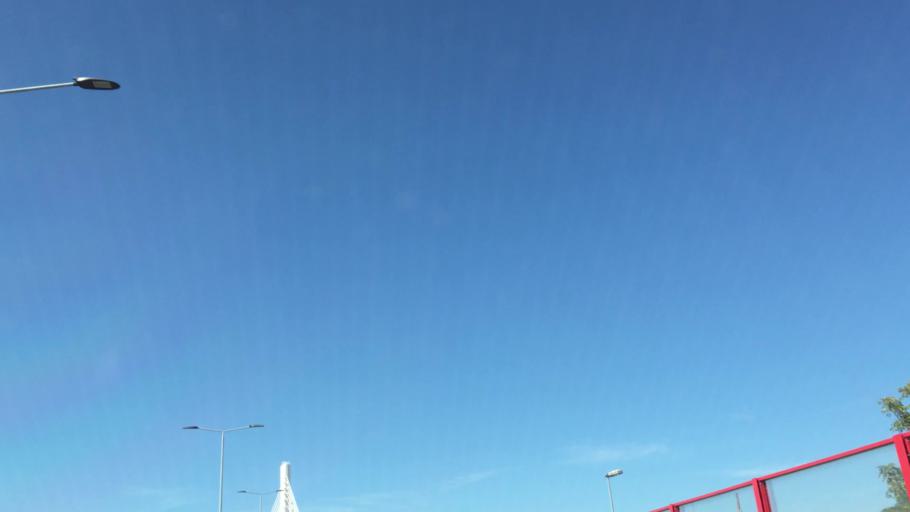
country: IT
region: Apulia
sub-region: Provincia di Bari
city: Bari
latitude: 41.1159
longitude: 16.8488
